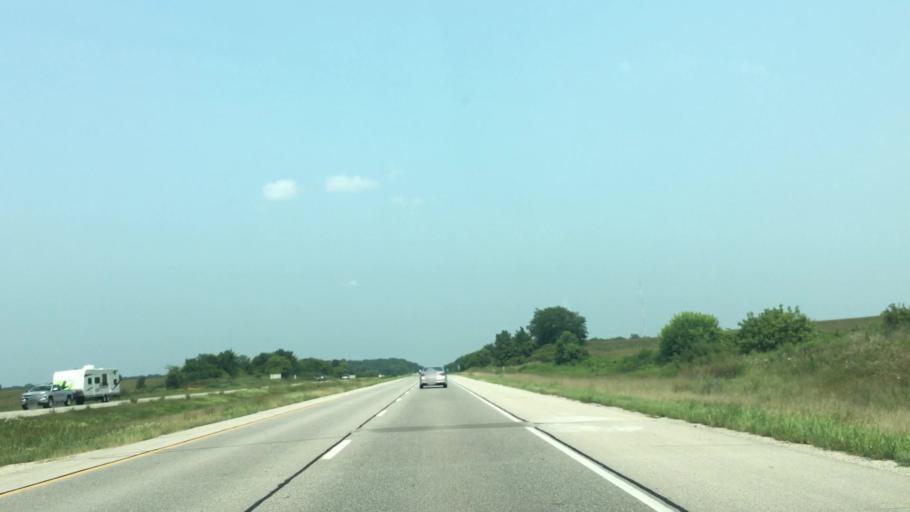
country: US
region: Iowa
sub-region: Linn County
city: Hiawatha
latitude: 42.0634
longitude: -91.7000
